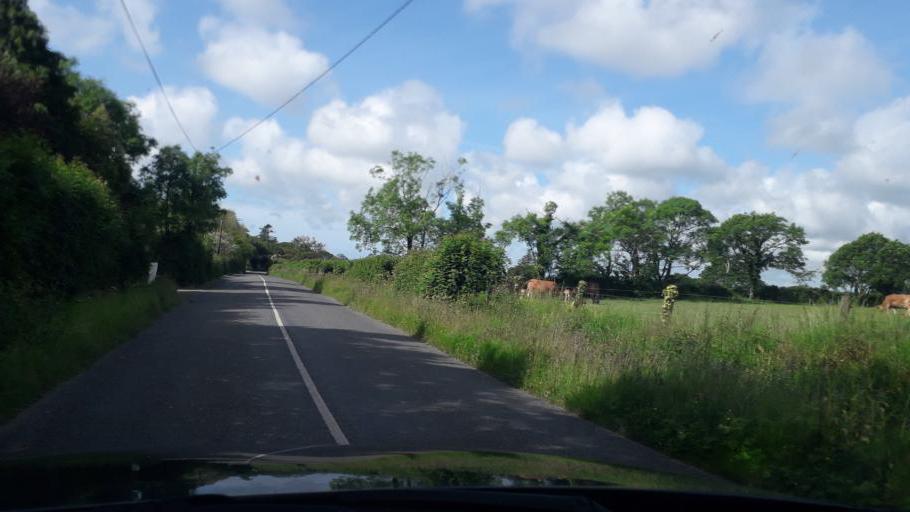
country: IE
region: Leinster
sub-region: Loch Garman
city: Loch Garman
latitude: 52.2792
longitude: -6.5406
